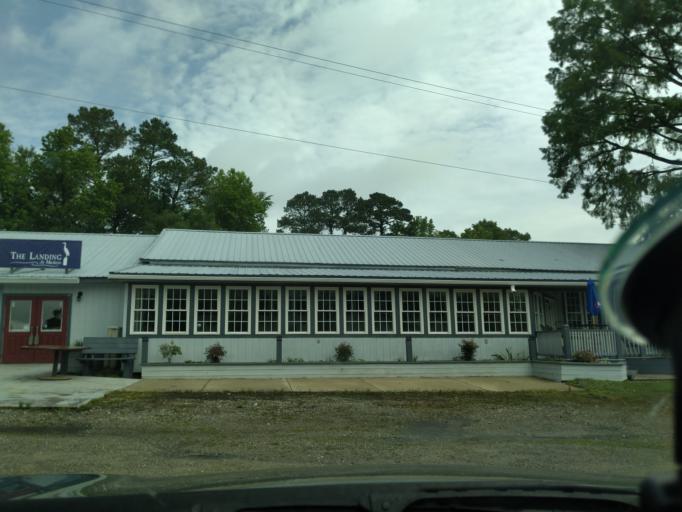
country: US
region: North Carolina
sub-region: Chowan County
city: Edenton
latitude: 35.9339
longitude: -76.6082
